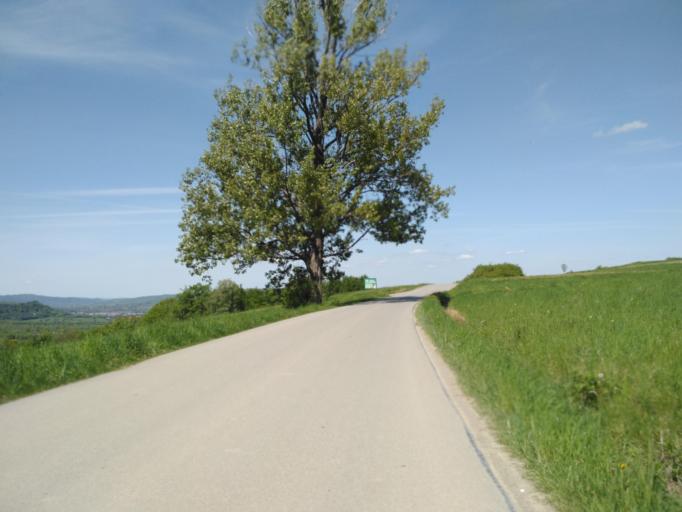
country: PL
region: Subcarpathian Voivodeship
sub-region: Powiat krosnienski
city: Iwonicz-Zdroj
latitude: 49.5374
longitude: 21.7477
